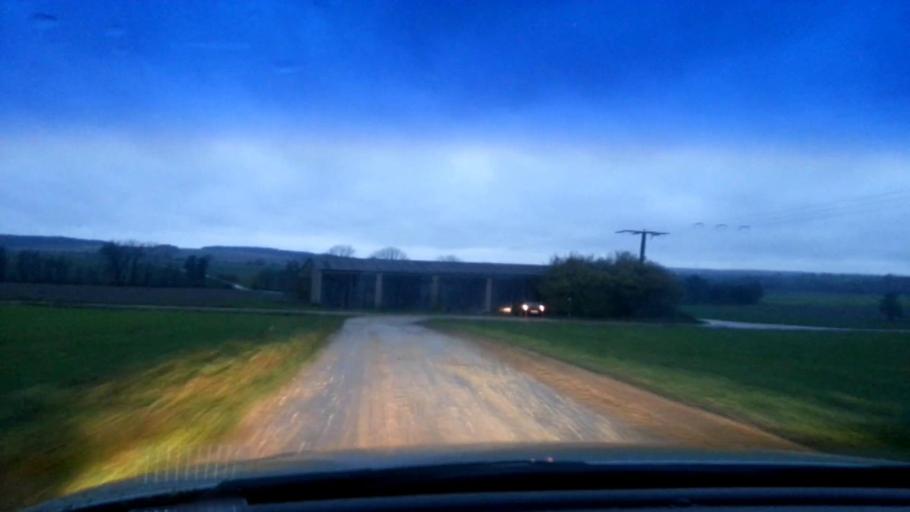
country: DE
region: Bavaria
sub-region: Upper Franconia
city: Schesslitz
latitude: 49.9502
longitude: 11.0104
